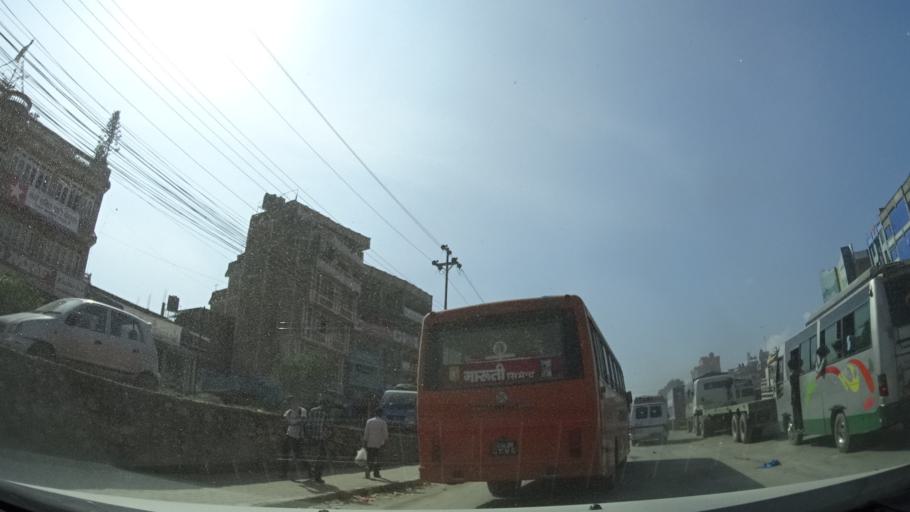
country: NP
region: Central Region
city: Kirtipur
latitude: 27.6975
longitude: 85.2816
